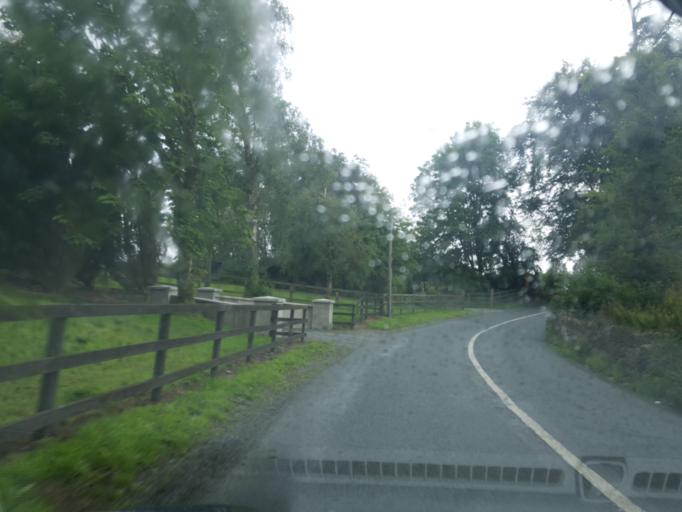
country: IE
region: Leinster
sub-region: Wicklow
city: Valleymount
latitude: 53.1295
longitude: -6.5901
